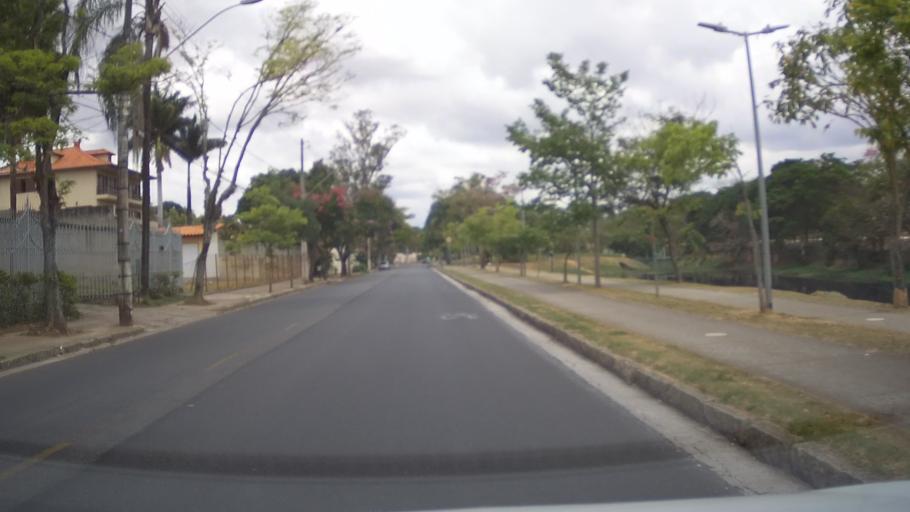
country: BR
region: Minas Gerais
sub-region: Belo Horizonte
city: Belo Horizonte
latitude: -19.8552
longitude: -43.9948
